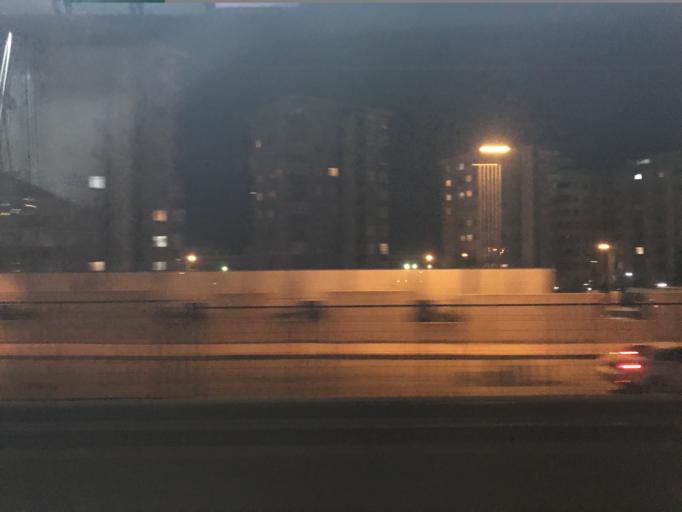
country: TR
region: Istanbul
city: Maltepe
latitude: 40.8934
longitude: 29.1754
